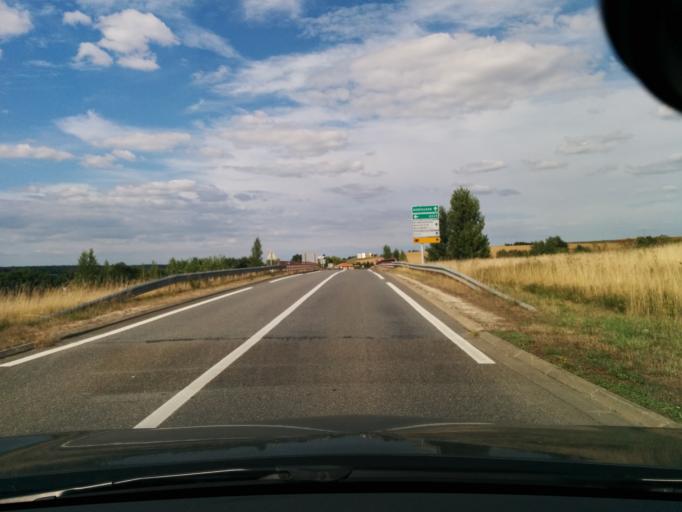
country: FR
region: Midi-Pyrenees
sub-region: Departement du Gers
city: Aubiet
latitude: 43.6543
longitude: 0.7829
